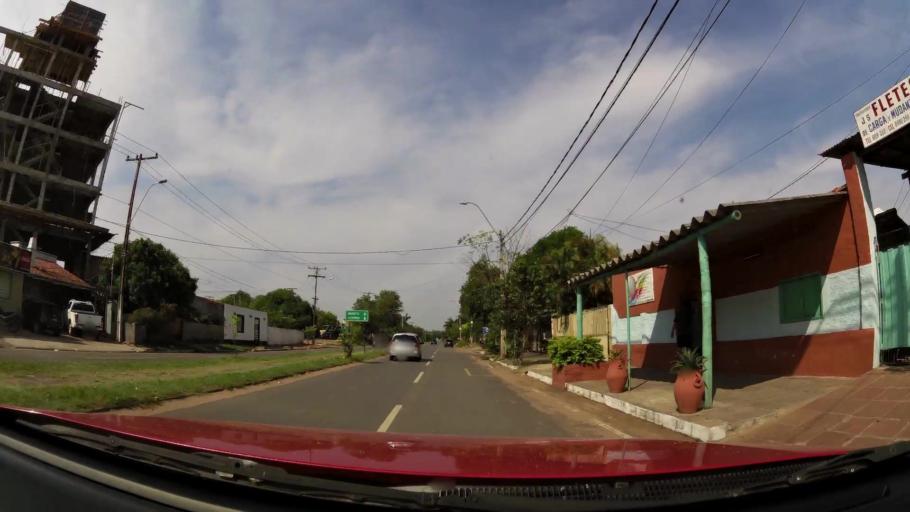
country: PY
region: Central
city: Fernando de la Mora
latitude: -25.2720
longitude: -57.5477
